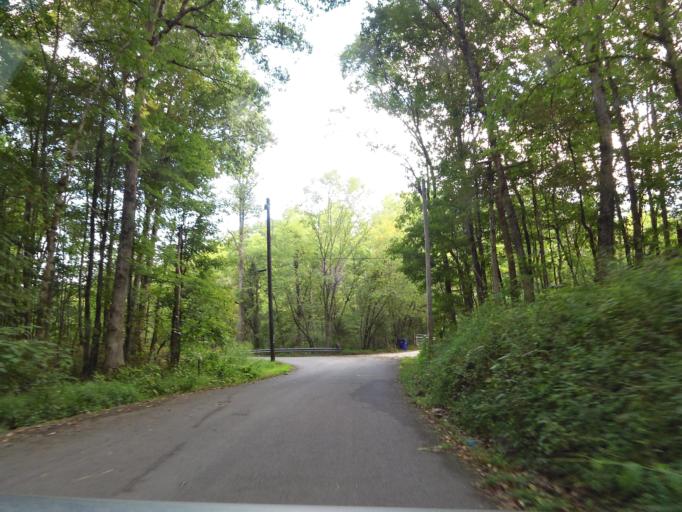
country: US
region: Tennessee
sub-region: Union County
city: Condon
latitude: 36.1217
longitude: -83.7729
